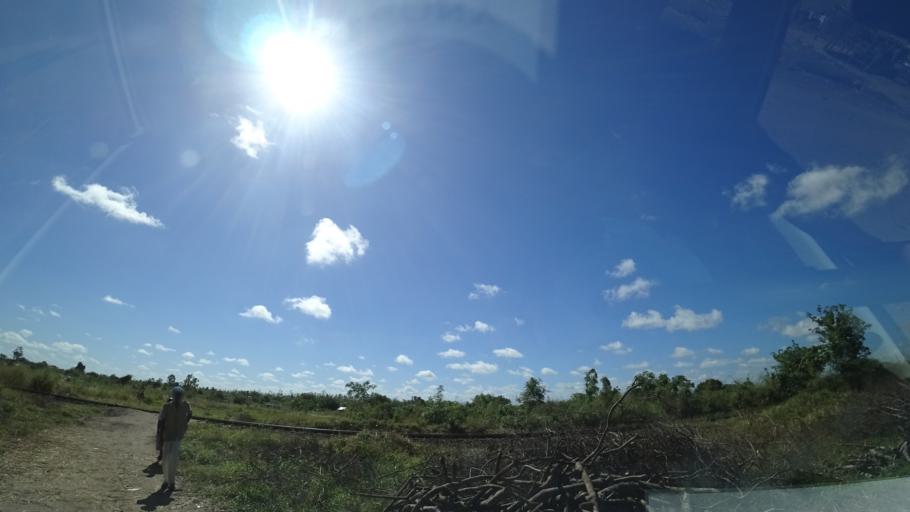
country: MZ
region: Sofala
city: Dondo
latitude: -19.2717
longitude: 34.6792
